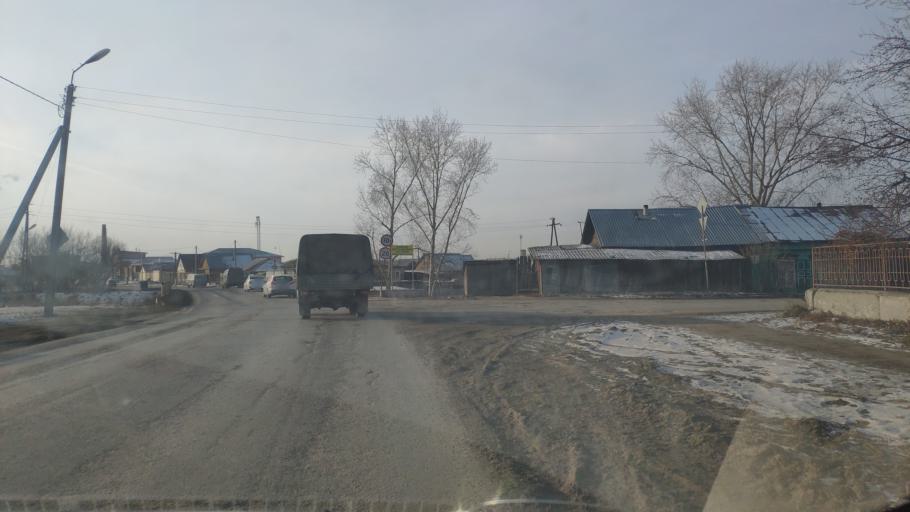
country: RU
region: Kurgan
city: Shadrinsk
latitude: 56.0898
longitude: 63.6770
